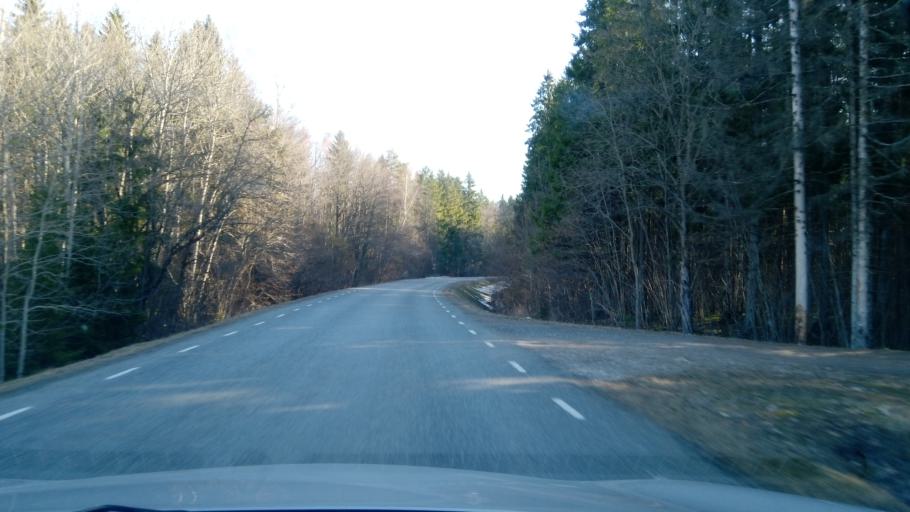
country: EE
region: Laeaene-Virumaa
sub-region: Kadrina vald
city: Kadrina
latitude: 59.2538
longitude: 26.2211
